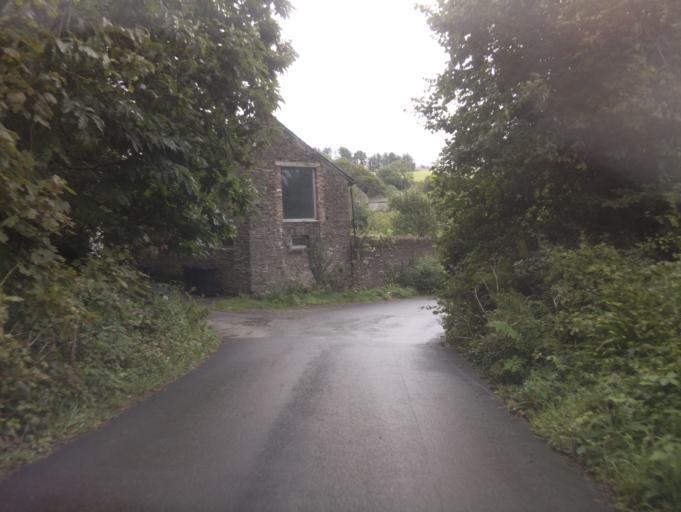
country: GB
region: England
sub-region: Devon
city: Kingsbridge
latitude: 50.3219
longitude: -3.7143
